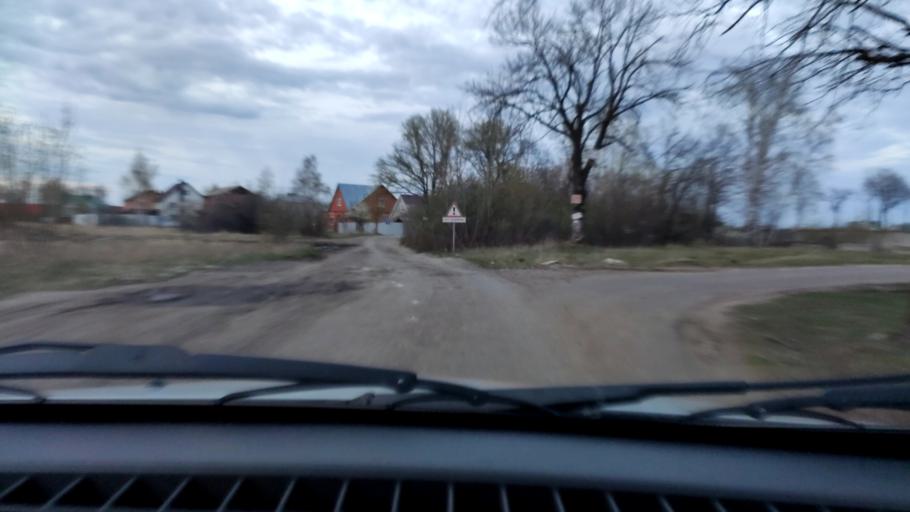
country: RU
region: Voronezj
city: Podgornoye
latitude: 51.7943
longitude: 39.2141
